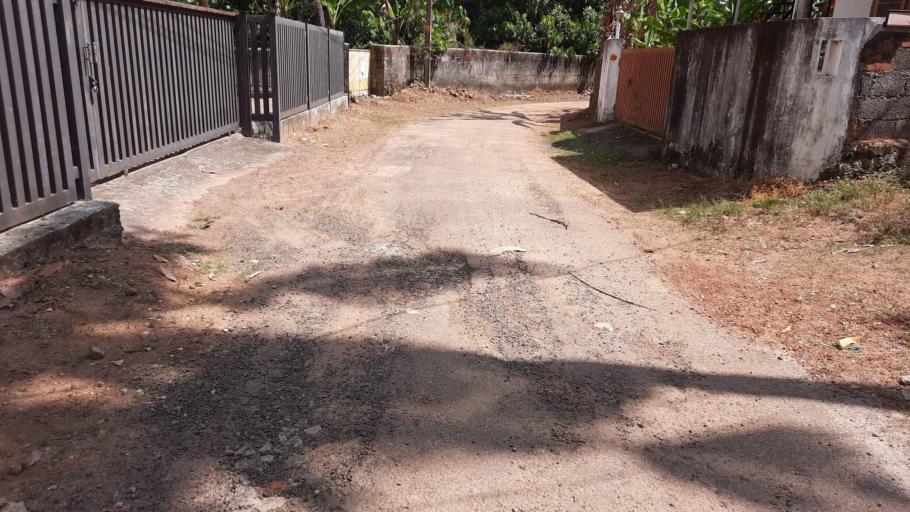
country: IN
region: Kerala
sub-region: Thiruvananthapuram
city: Thiruvananthapuram
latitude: 8.5558
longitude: 76.9305
